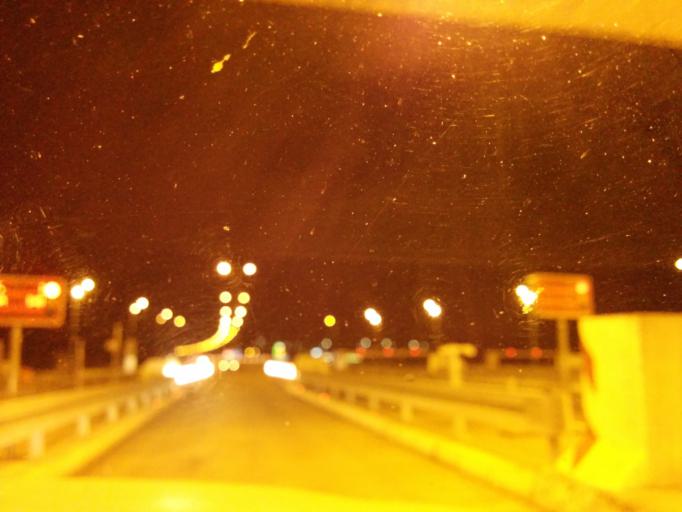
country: RS
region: Autonomna Pokrajina Vojvodina
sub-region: Sremski Okrug
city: Sid
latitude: 45.0484
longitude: 19.1924
